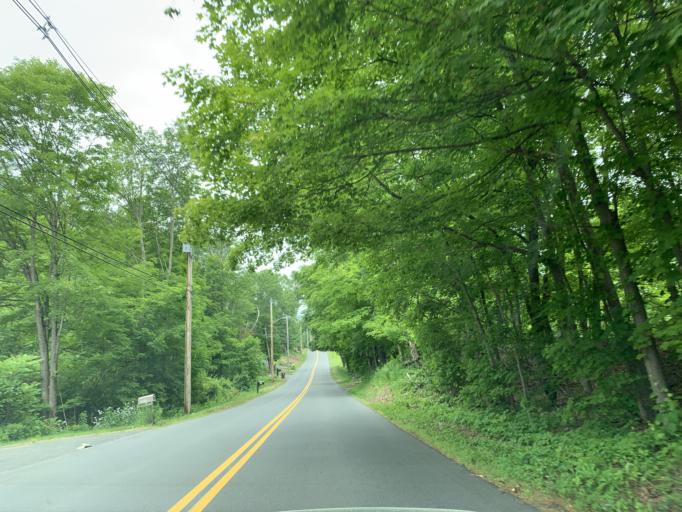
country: US
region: Massachusetts
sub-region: Hampshire County
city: Southampton
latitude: 42.1881
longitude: -72.7577
